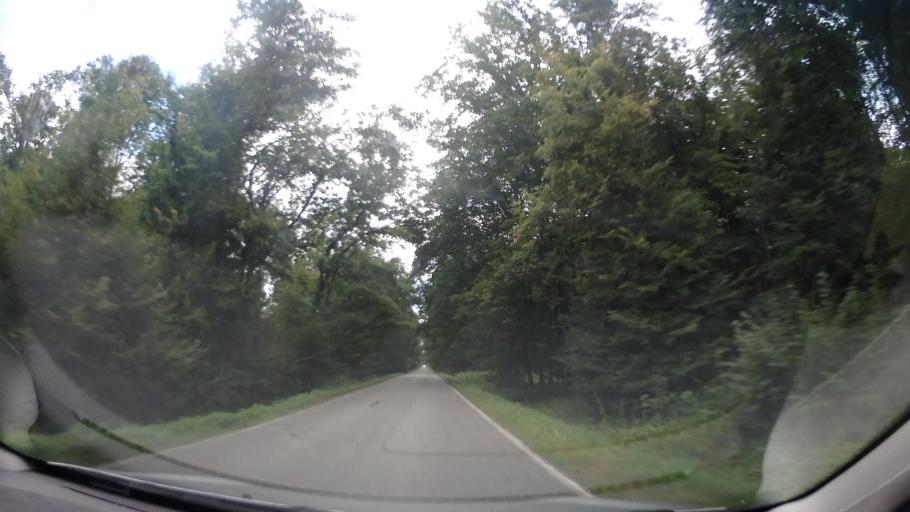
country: CZ
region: Olomoucky
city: Bila Lhota
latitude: 49.7131
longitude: 17.0231
